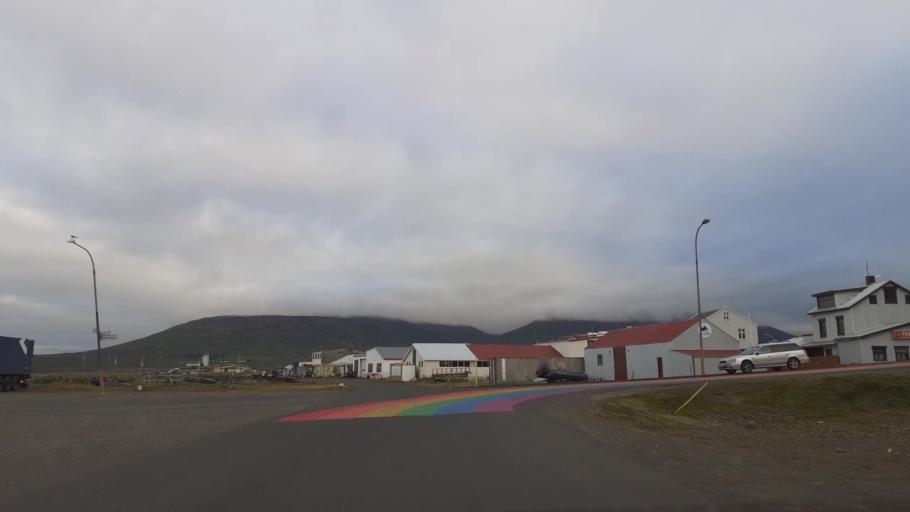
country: IS
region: Northeast
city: Dalvik
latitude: 65.9710
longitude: -18.5276
